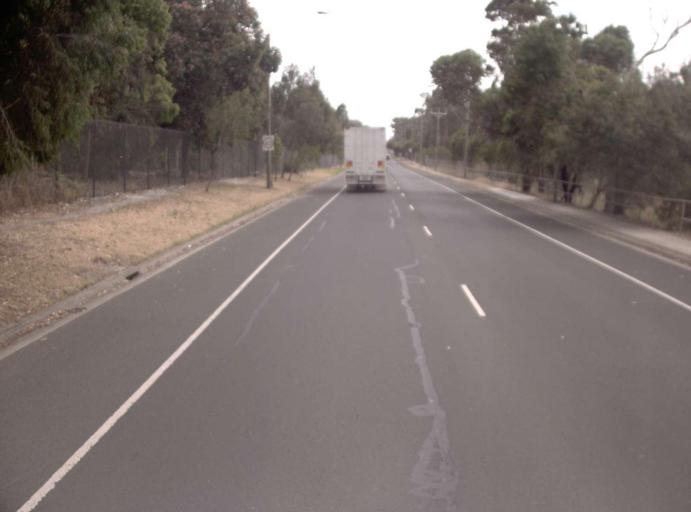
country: AU
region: Victoria
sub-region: Monash
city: Oakleigh South
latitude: -37.9254
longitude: 145.1008
